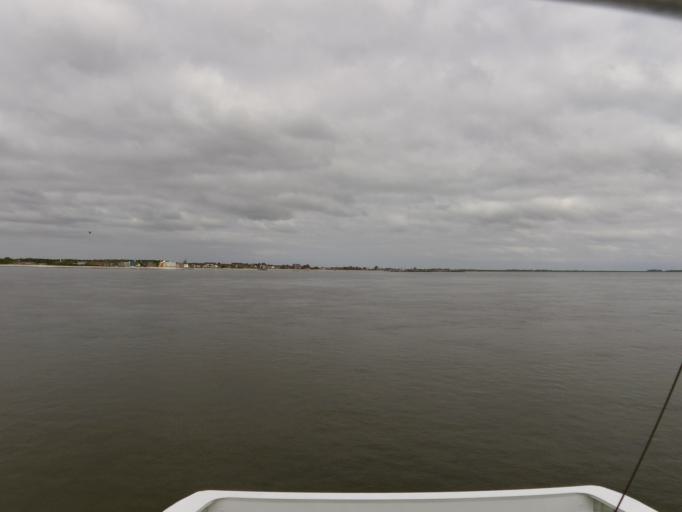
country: DE
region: Schleswig-Holstein
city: Wyk auf Fohr
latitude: 54.6790
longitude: 8.5915
